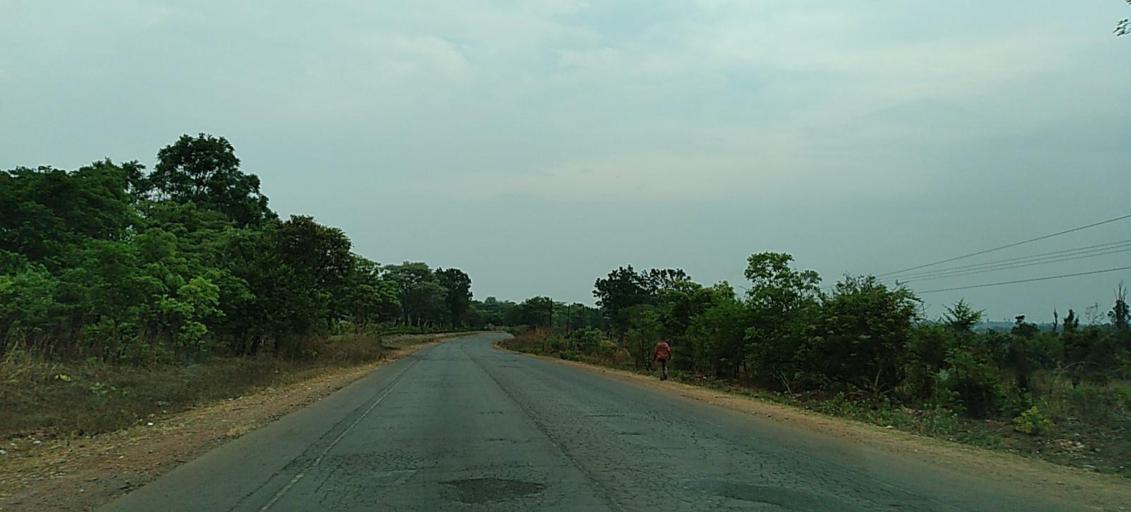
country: ZM
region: Copperbelt
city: Luanshya
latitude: -13.0946
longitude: 28.4313
